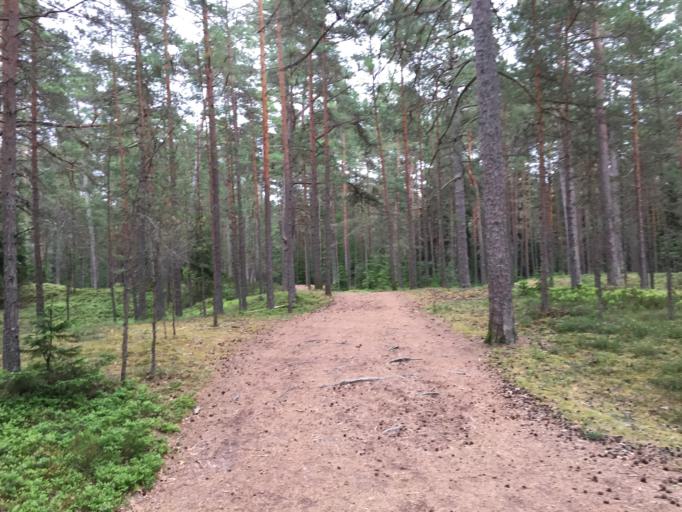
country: LV
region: Carnikava
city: Carnikava
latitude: 57.1206
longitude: 24.2193
